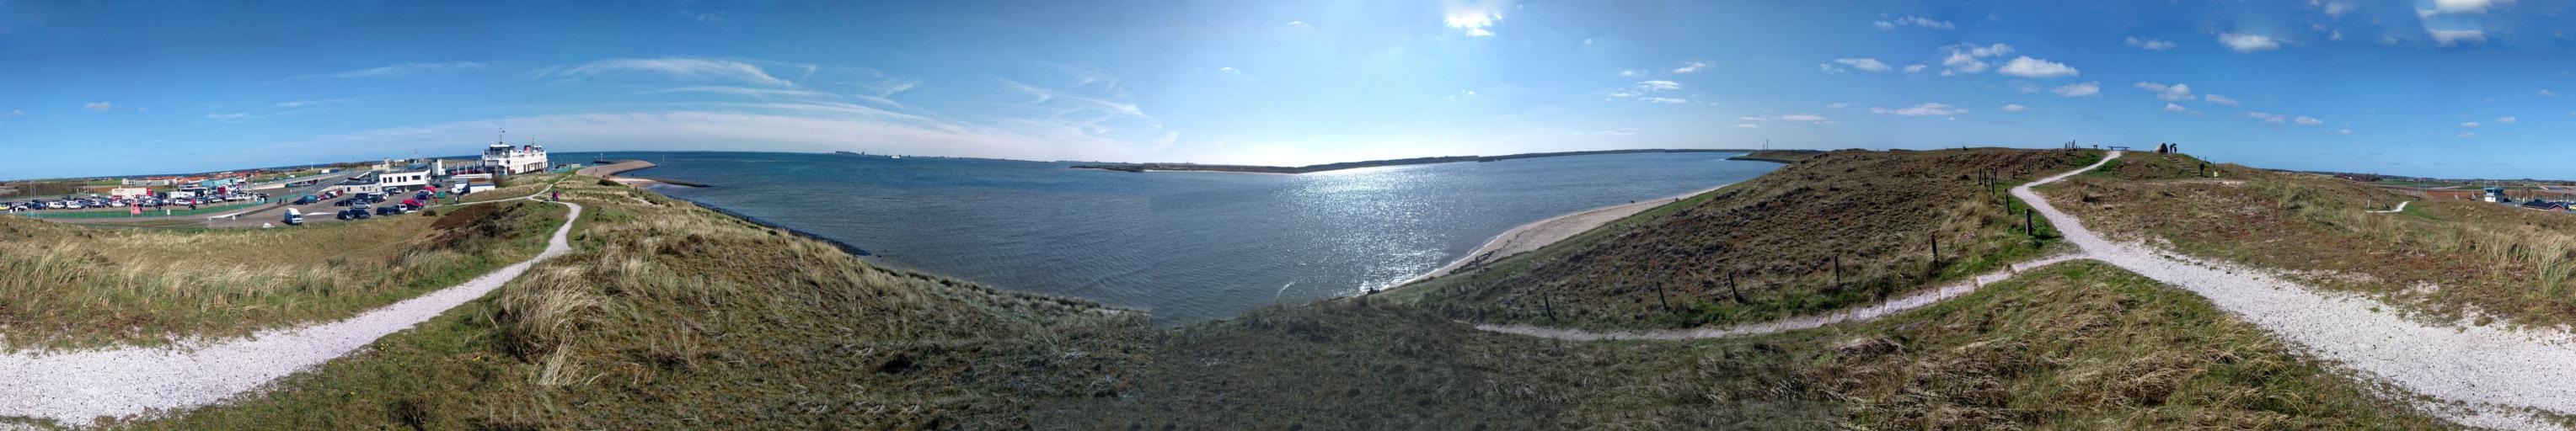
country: NL
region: North Holland
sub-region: Gemeente Den Helder
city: Den Helder
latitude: 53.0043
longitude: 4.7773
